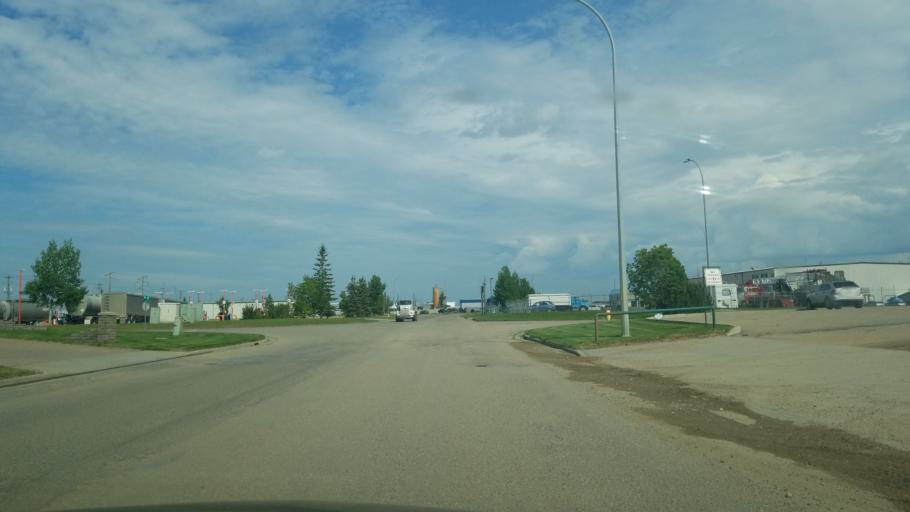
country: CA
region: Saskatchewan
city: Lloydminster
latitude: 53.2914
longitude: -110.0376
